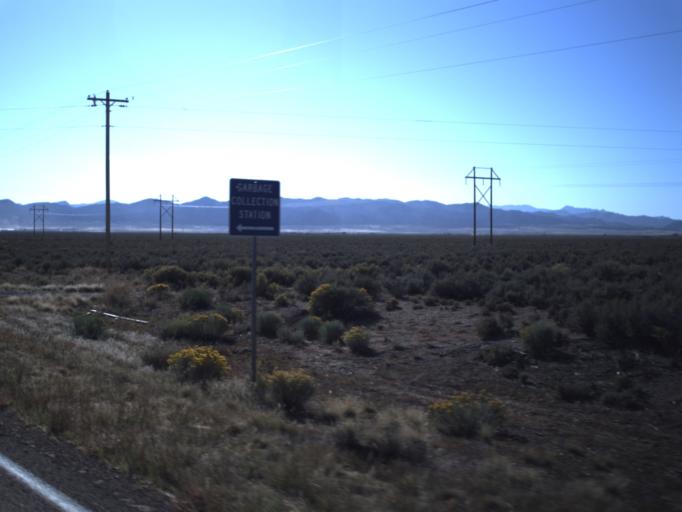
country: US
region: Utah
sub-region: Washington County
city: Enterprise
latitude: 37.7051
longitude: -113.6440
